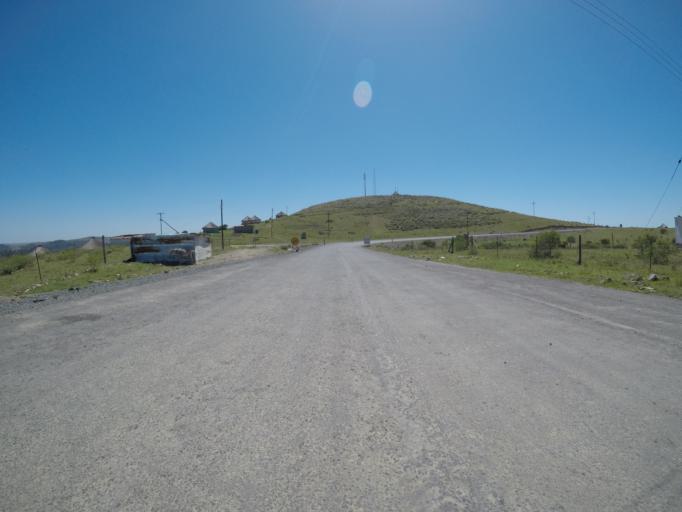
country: ZA
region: Eastern Cape
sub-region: OR Tambo District Municipality
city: Libode
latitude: -32.0012
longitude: 29.1169
